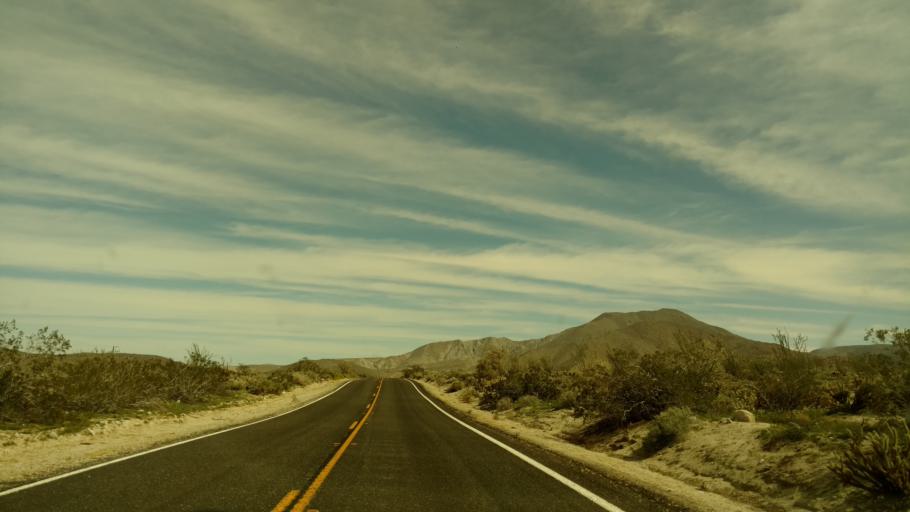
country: US
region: California
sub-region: San Diego County
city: Borrego Springs
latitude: 33.1340
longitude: -116.3415
